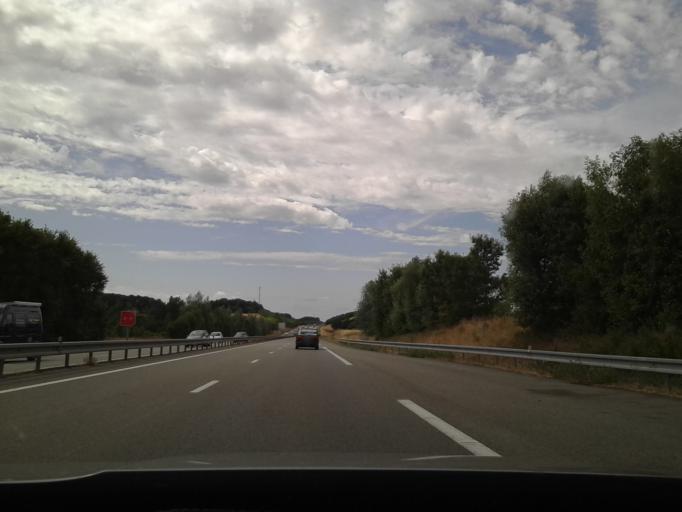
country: FR
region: Pays de la Loire
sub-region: Departement de la Sarthe
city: Sainte-Jamme-sur-Sarthe
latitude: 48.1555
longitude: 0.1427
